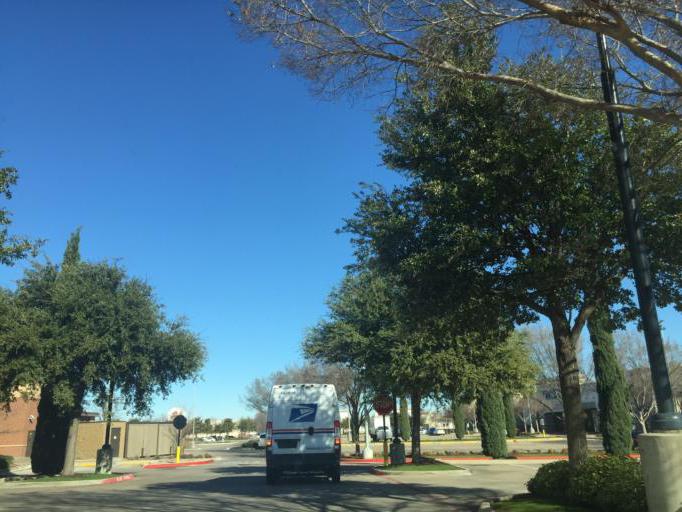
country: US
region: Texas
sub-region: Tarrant County
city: Fort Worth
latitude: 32.7527
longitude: -97.3525
